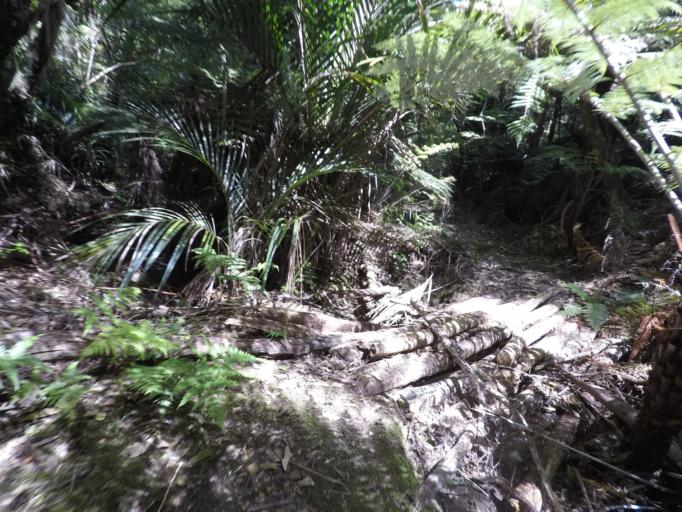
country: NZ
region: Auckland
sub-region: Auckland
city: Titirangi
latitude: -36.9743
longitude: 174.6307
